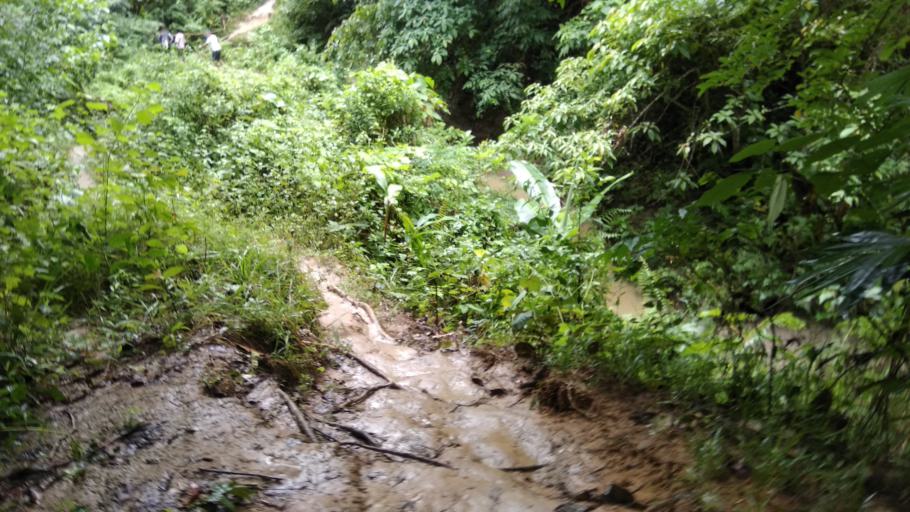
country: IN
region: Tripura
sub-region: Dhalai
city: Kamalpur
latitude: 24.1720
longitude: 91.8888
